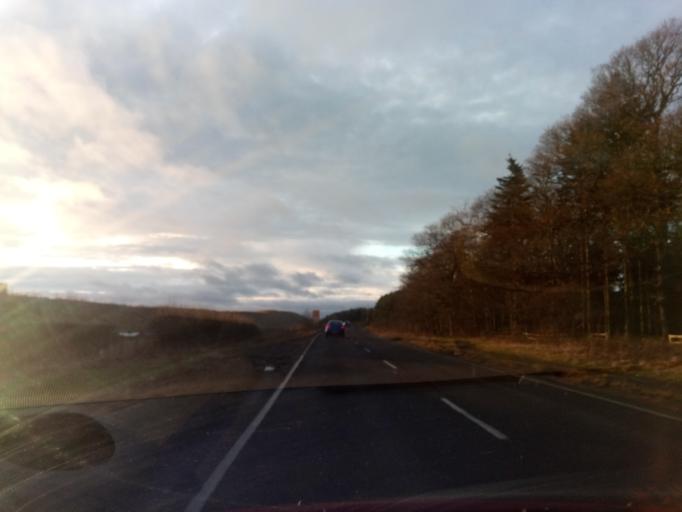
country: GB
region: England
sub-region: Newcastle upon Tyne
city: Dinnington
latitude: 55.0790
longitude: -1.6557
